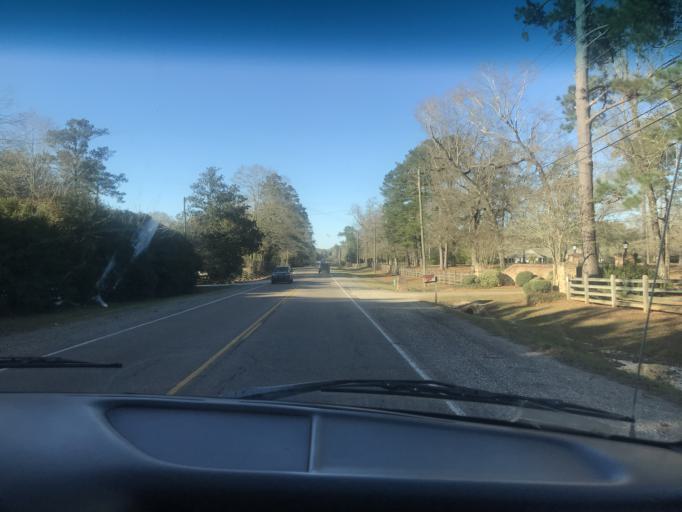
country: US
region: Louisiana
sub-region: Saint Tammany Parish
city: Covington
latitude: 30.6032
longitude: -90.1808
